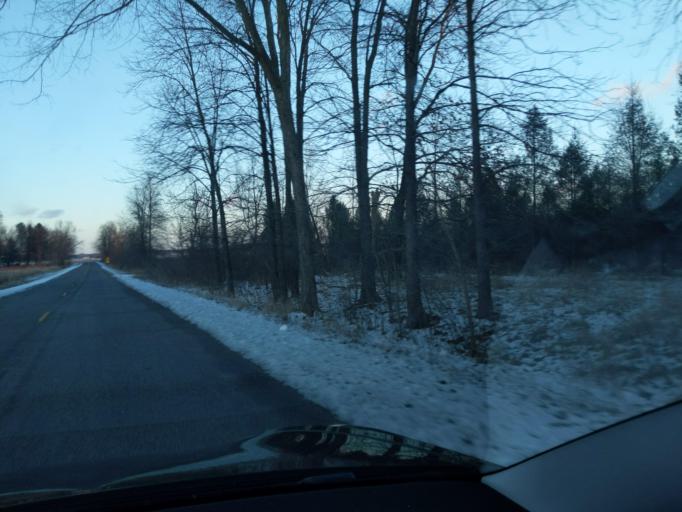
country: US
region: Michigan
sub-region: Ingham County
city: Stockbridge
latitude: 42.4648
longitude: -84.2779
